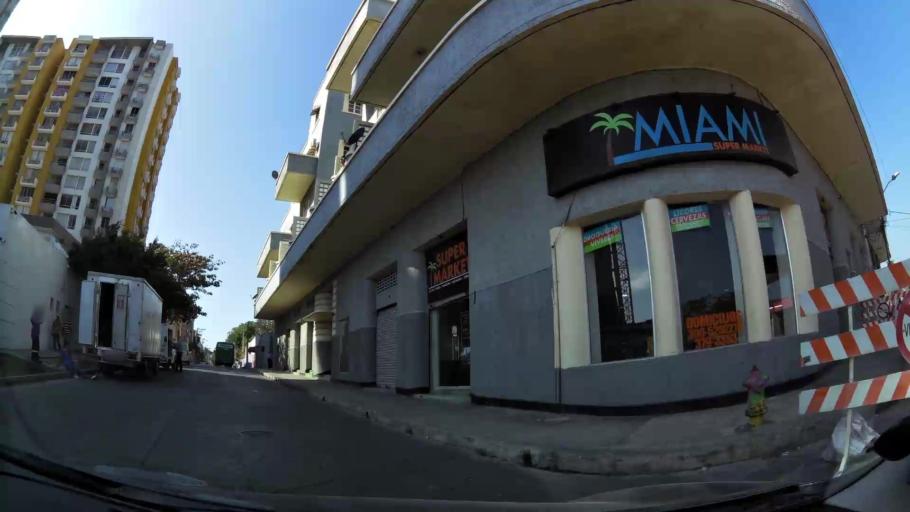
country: CO
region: Atlantico
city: Barranquilla
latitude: 10.9867
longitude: -74.7865
